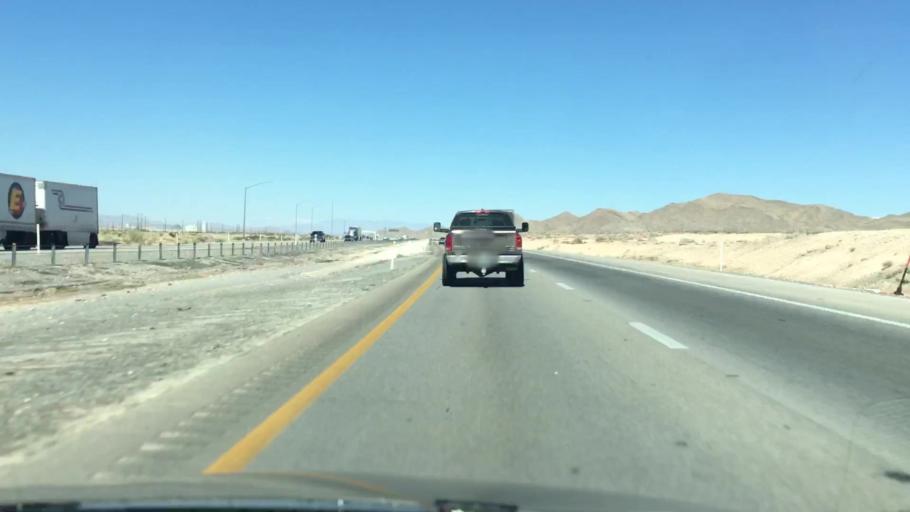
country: US
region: Nevada
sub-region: Clark County
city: Nellis Air Force Base
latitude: 36.3304
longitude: -114.9232
